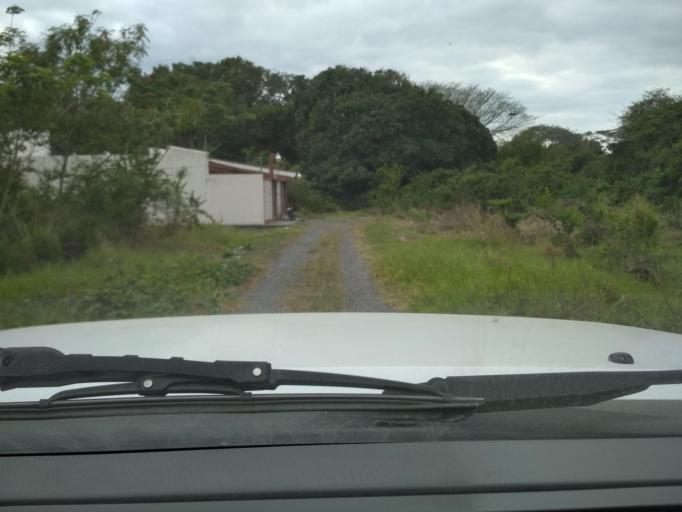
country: MX
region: Veracruz
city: El Tejar
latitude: 19.0721
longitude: -96.1431
